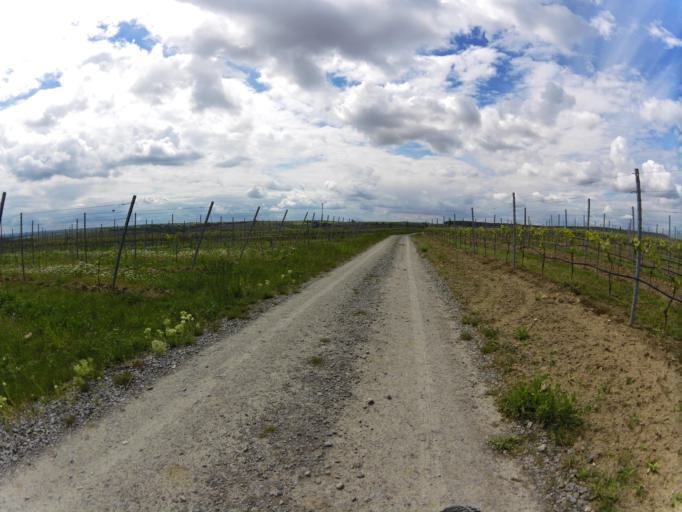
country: DE
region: Bavaria
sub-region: Regierungsbezirk Unterfranken
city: Sommerach
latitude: 49.8410
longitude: 10.1975
